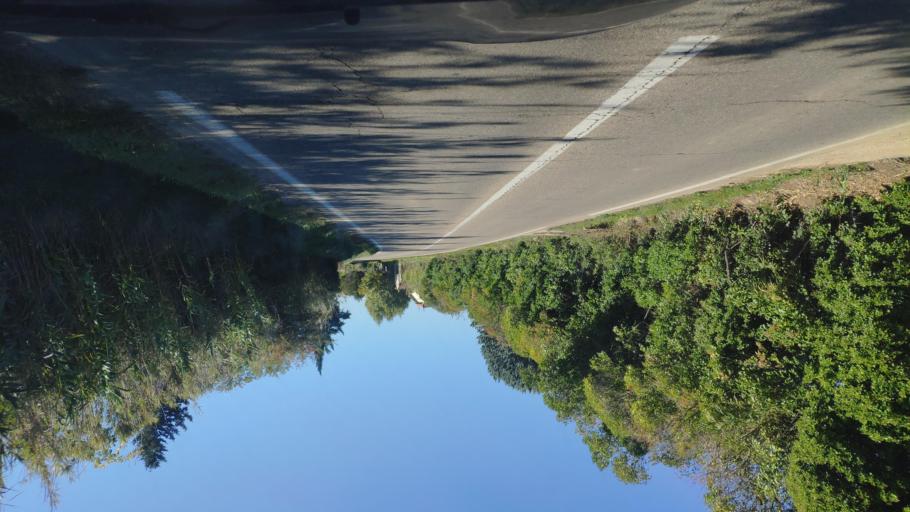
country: FR
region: Provence-Alpes-Cote d'Azur
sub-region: Departement du Vaucluse
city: Carpentras
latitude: 44.0678
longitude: 5.0275
